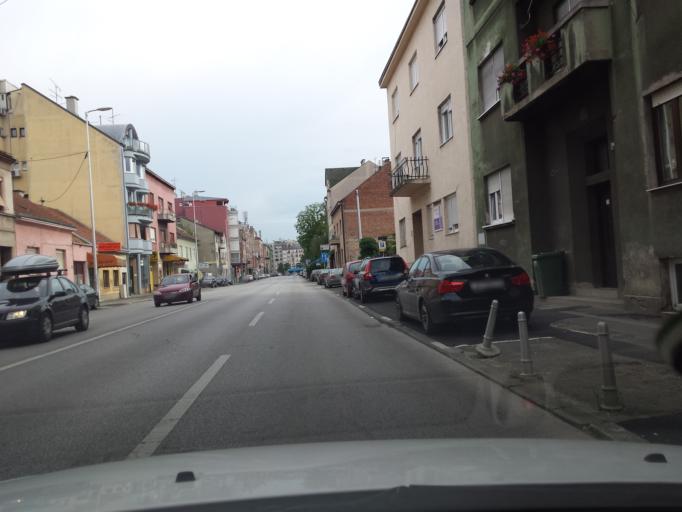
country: HR
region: Grad Zagreb
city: Zagreb - Centar
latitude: 45.8030
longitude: 15.9550
